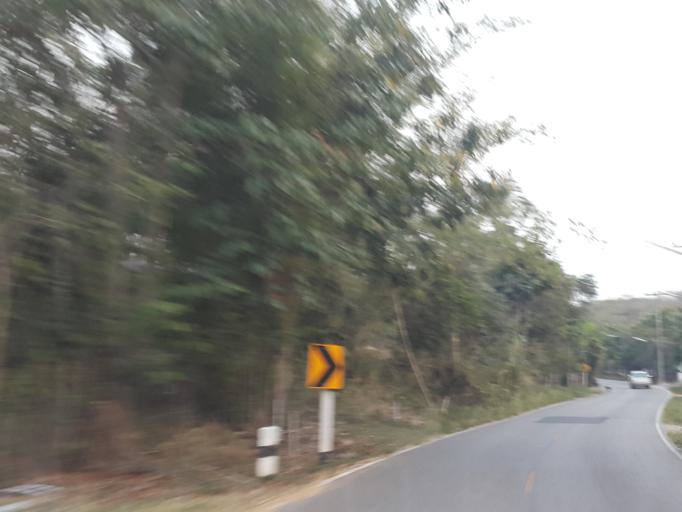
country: TH
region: Chiang Mai
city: Mae Taeng
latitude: 18.9892
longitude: 98.9019
